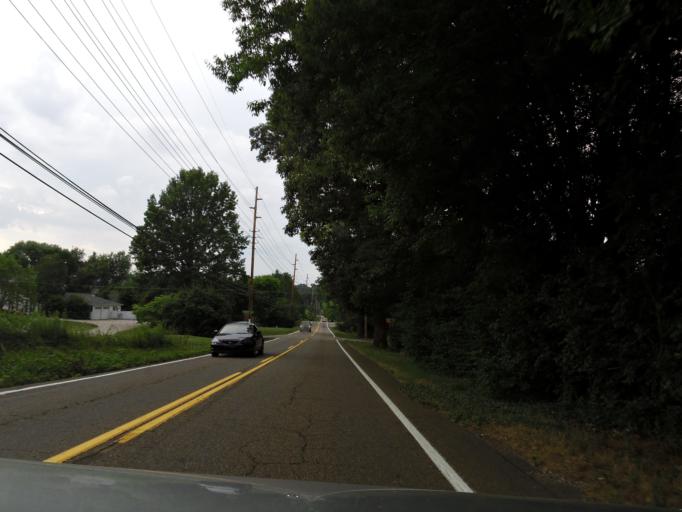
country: US
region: Tennessee
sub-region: Knox County
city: Farragut
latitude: 35.8584
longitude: -84.1128
